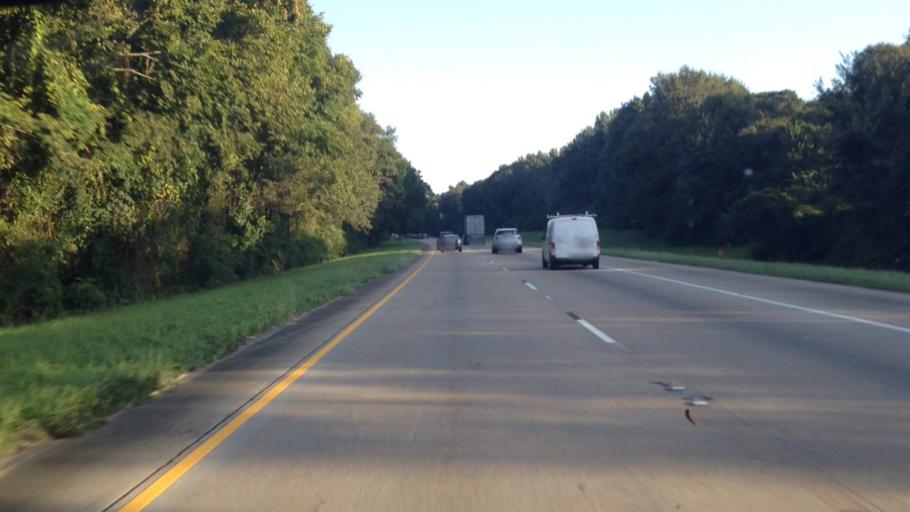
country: US
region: Louisiana
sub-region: Ascension Parish
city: Prairieville
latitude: 30.3062
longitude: -90.9936
